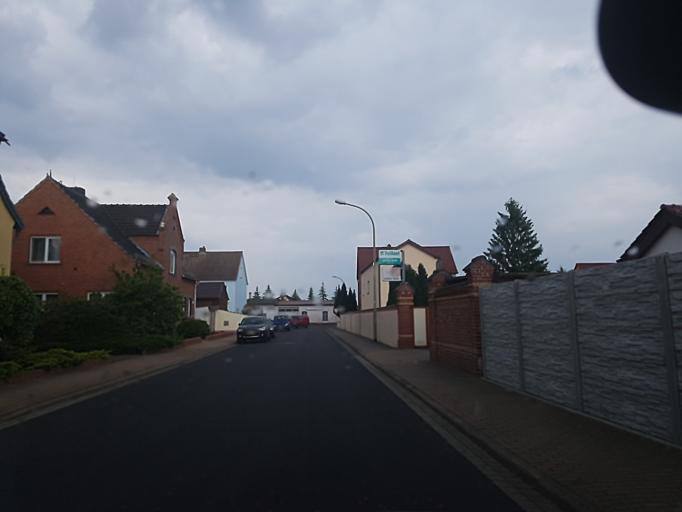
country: DE
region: Saxony-Anhalt
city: Elster
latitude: 51.8299
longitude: 12.8281
